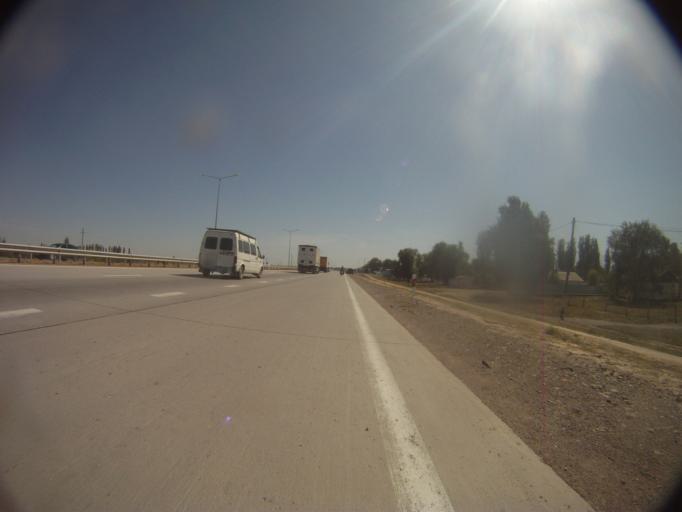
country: KZ
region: Zhambyl
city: Merke
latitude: 42.8757
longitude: 73.1187
